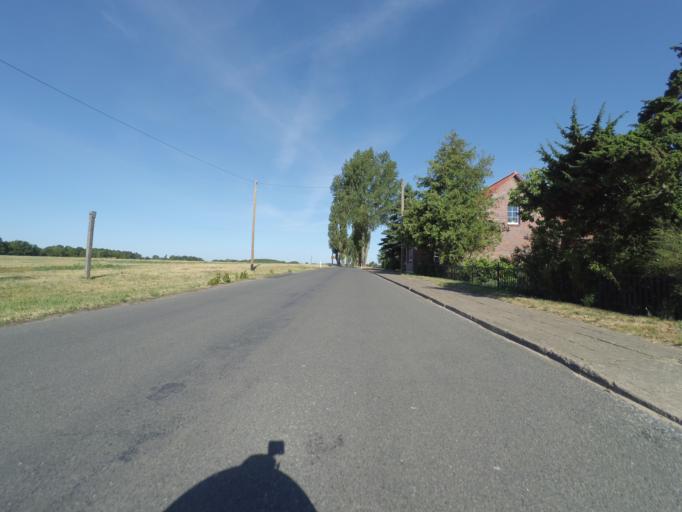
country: DE
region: Mecklenburg-Vorpommern
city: Lubz
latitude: 53.3685
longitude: 12.0948
